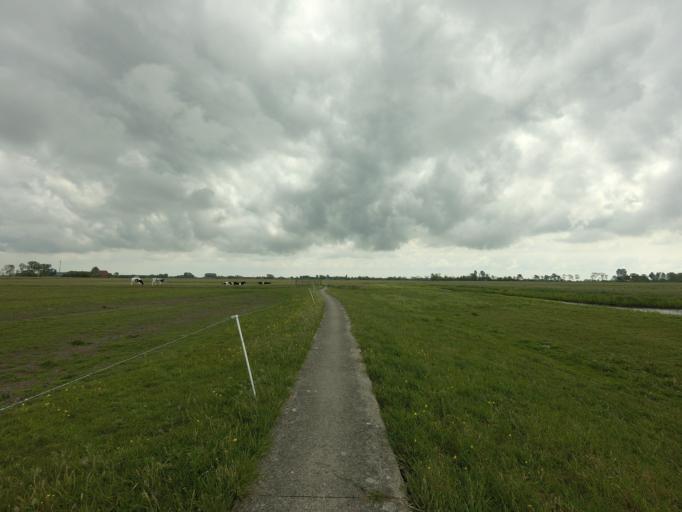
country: NL
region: Friesland
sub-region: Gemeente Littenseradiel
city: Wommels
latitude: 53.1106
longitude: 5.6034
